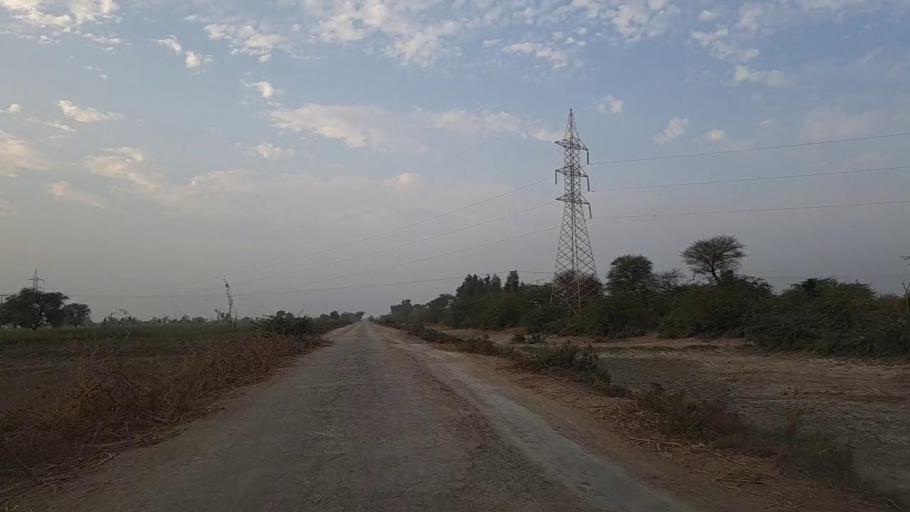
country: PK
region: Sindh
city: Mirwah Gorchani
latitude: 25.3144
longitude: 69.2236
